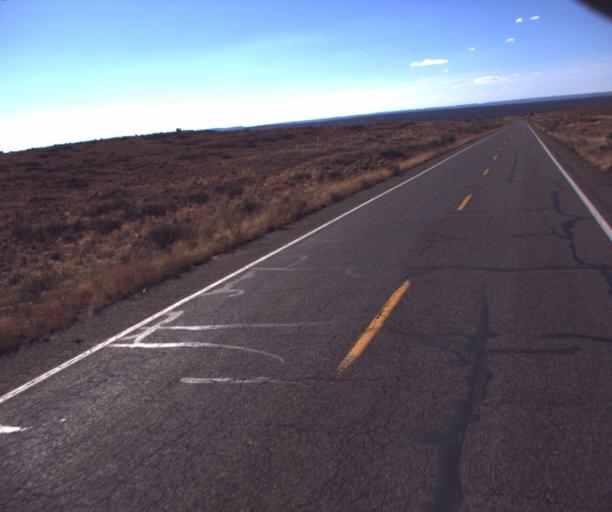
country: US
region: Arizona
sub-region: Coconino County
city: Kaibito
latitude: 36.6126
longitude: -111.0391
